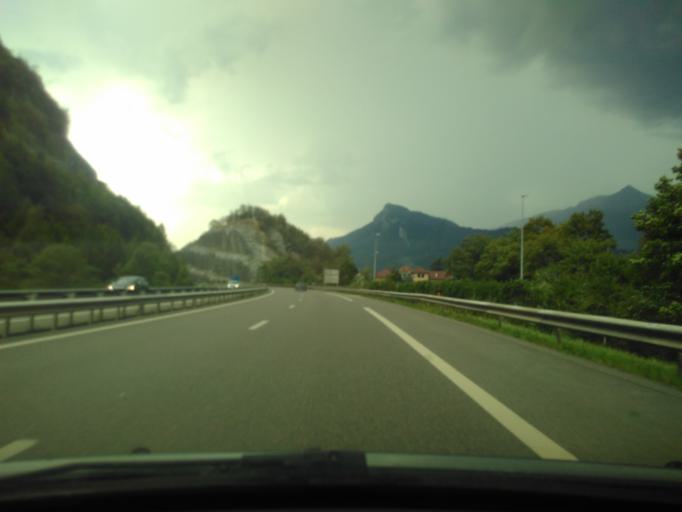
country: FR
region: Rhone-Alpes
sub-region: Departement de la Haute-Savoie
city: Cluses
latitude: 46.0532
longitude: 6.5818
